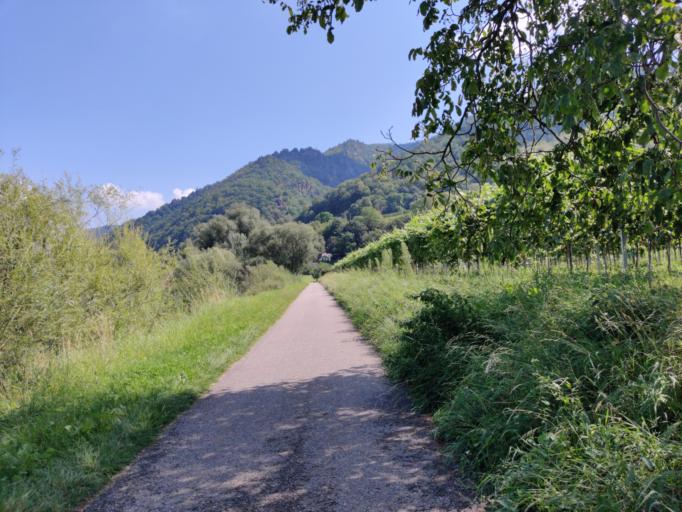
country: AT
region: Lower Austria
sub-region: Politischer Bezirk Krems
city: Spitz
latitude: 48.3701
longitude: 15.4453
